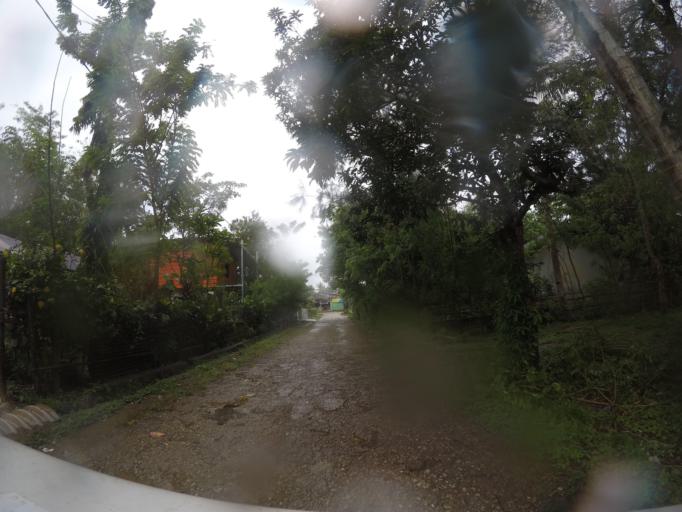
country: TL
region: Lautem
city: Lospalos
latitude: -8.5199
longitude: 126.9996
